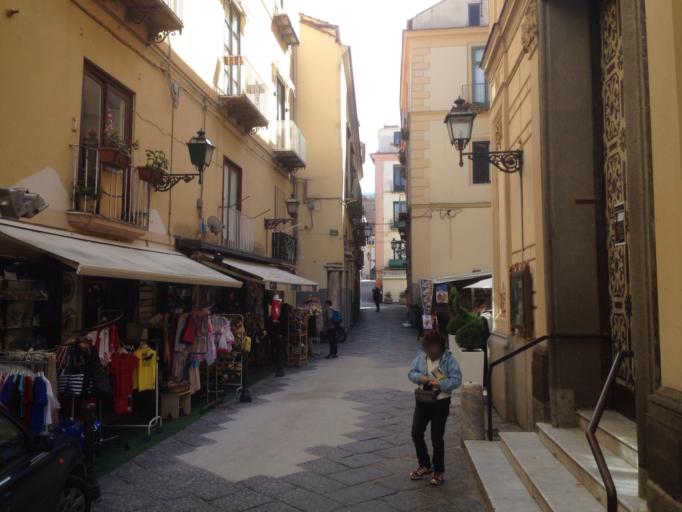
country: IT
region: Campania
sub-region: Provincia di Napoli
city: Sorrento
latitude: 40.6264
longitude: 14.3719
